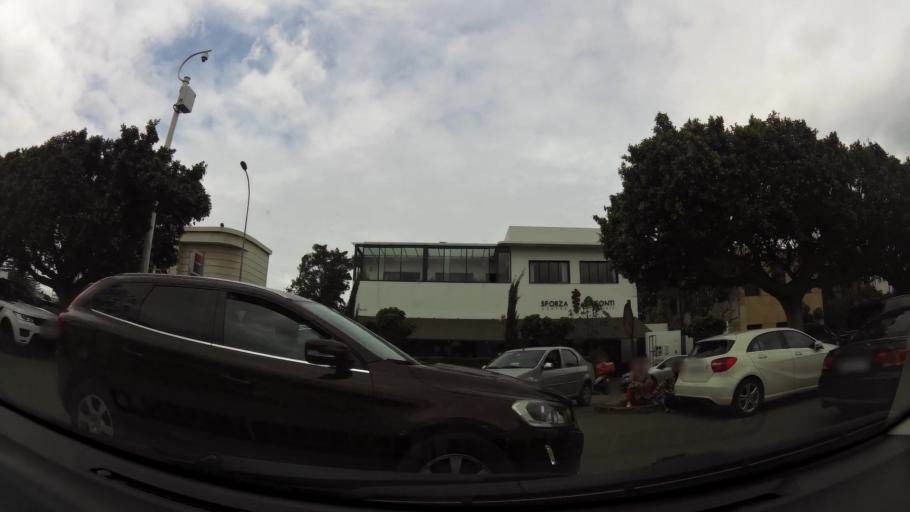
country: MA
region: Grand Casablanca
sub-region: Casablanca
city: Casablanca
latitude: 33.5726
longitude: -7.6570
